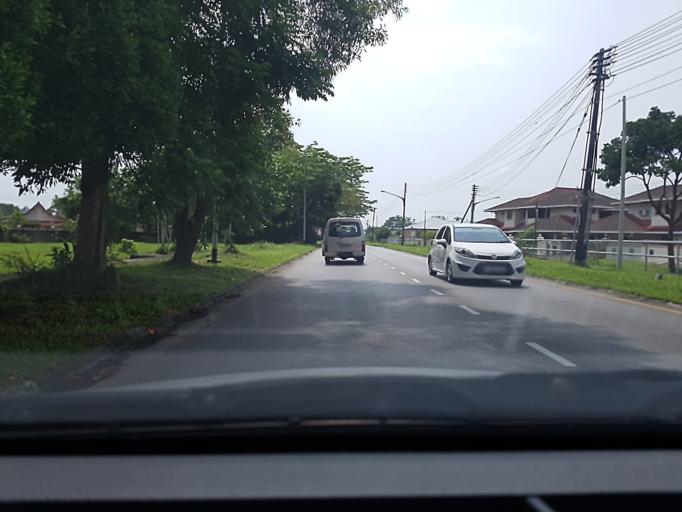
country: MY
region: Sarawak
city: Kuching
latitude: 1.5232
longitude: 110.3712
